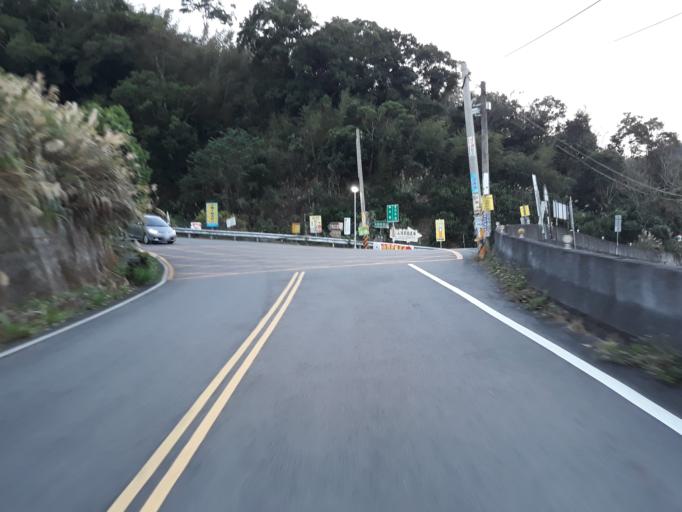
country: TW
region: Taiwan
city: Fengyuan
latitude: 24.3732
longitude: 120.8636
